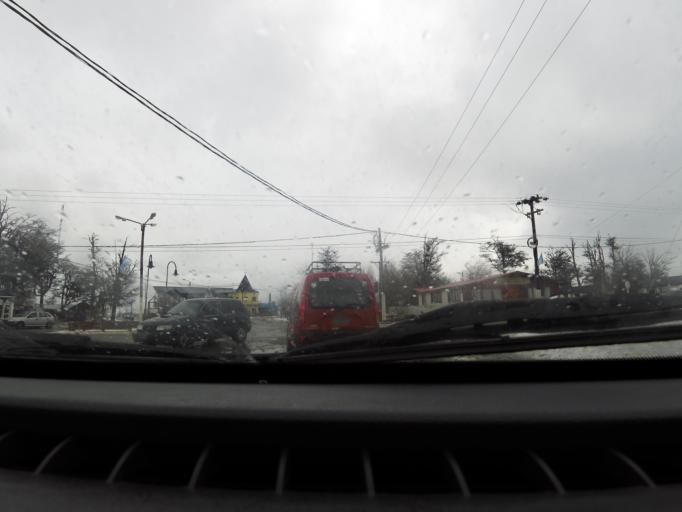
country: AR
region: Tierra del Fuego
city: Rio Grande
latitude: -54.5103
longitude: -67.1951
